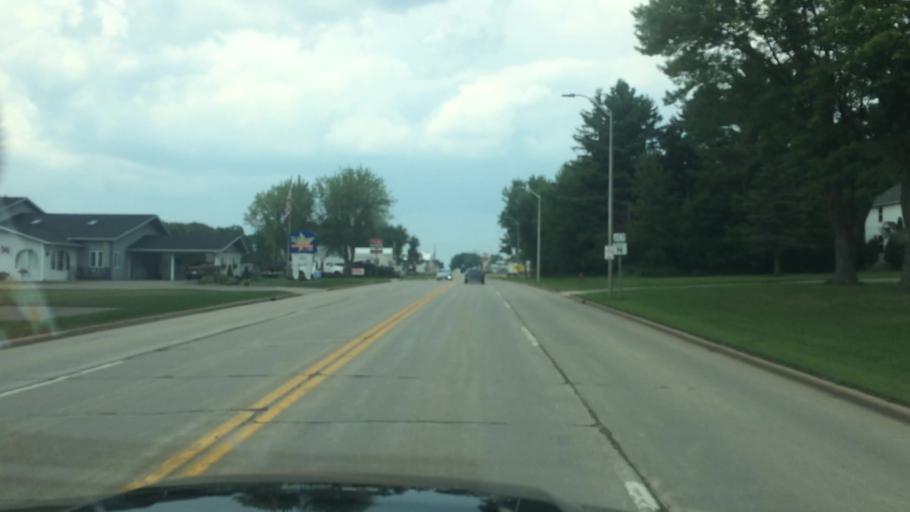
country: US
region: Wisconsin
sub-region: Clark County
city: Colby
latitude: 44.8993
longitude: -90.3150
